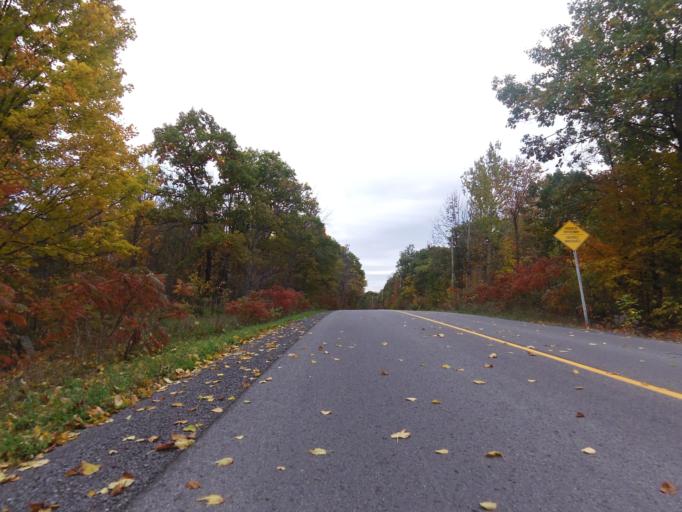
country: CA
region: Ontario
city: Arnprior
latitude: 45.4225
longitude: -76.0954
